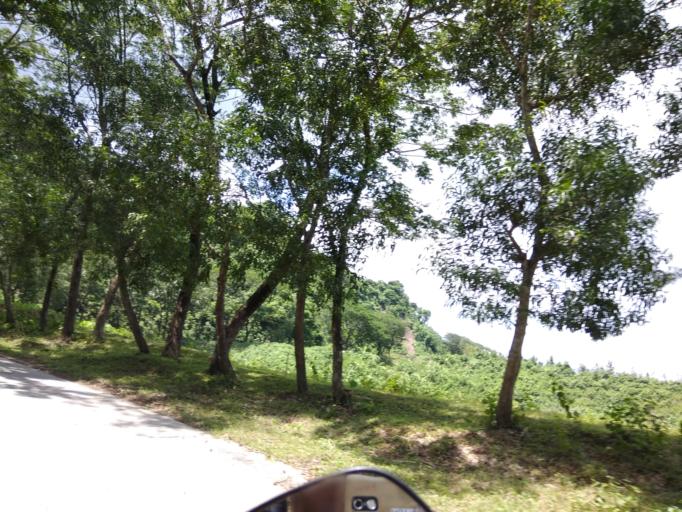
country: BD
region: Chittagong
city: Cox's Bazar
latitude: 21.6654
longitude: 92.3526
